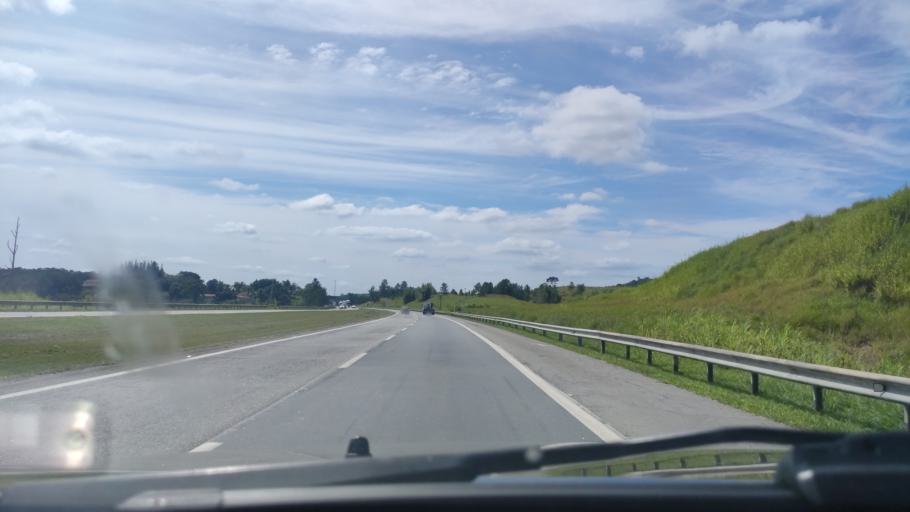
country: BR
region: Sao Paulo
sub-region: Santa Isabel
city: Santa Isabel
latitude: -23.4118
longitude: -46.1872
